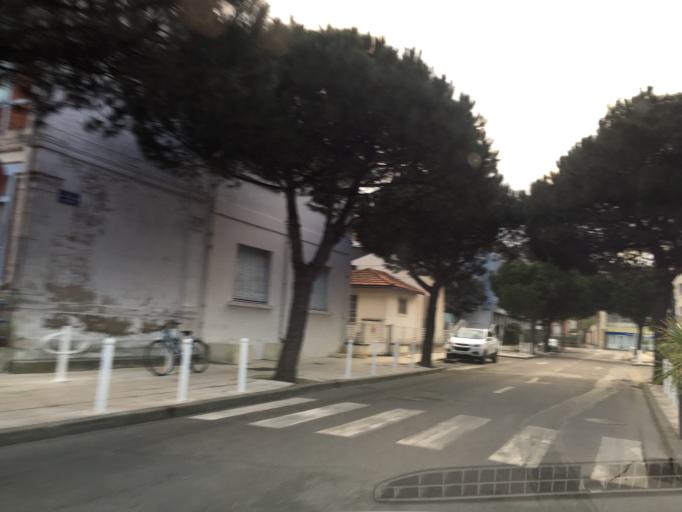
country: FR
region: Aquitaine
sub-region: Departement de la Gironde
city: Arcachon
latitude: 44.6636
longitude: -1.1638
